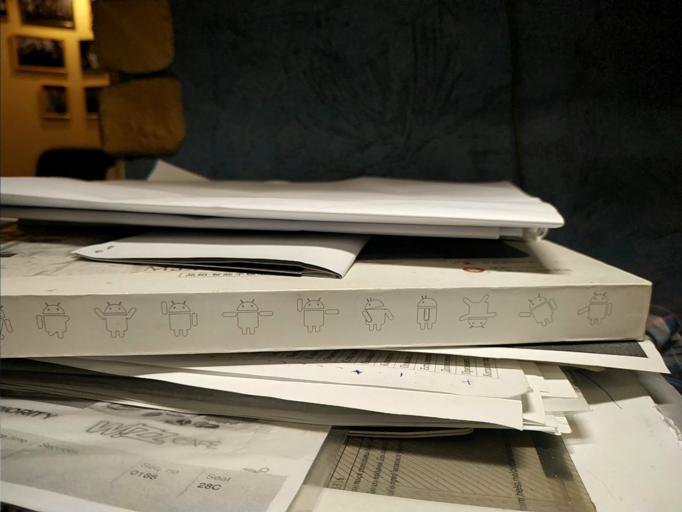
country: RU
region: Tverskaya
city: Zubtsov
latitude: 56.0802
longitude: 34.8025
